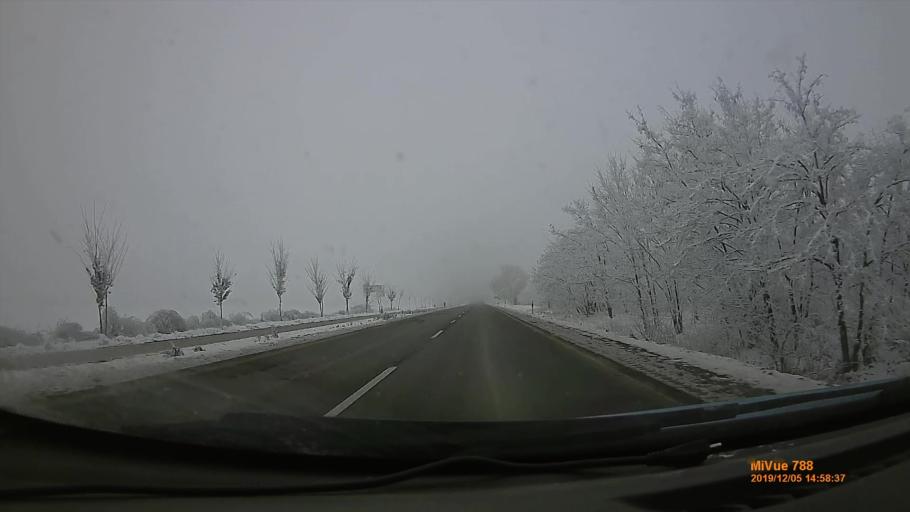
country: HU
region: Szabolcs-Szatmar-Bereg
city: Nyirtelek
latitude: 48.0501
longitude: 21.5689
